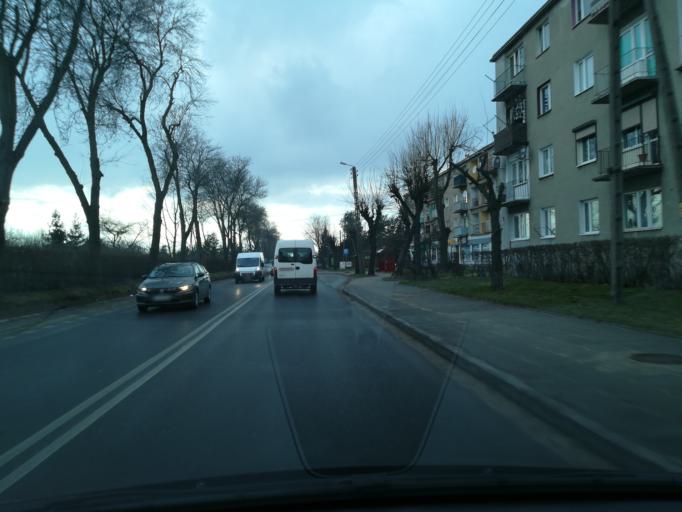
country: PL
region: Lodz Voivodeship
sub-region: Powiat radomszczanski
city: Radomsko
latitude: 51.0717
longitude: 19.4236
